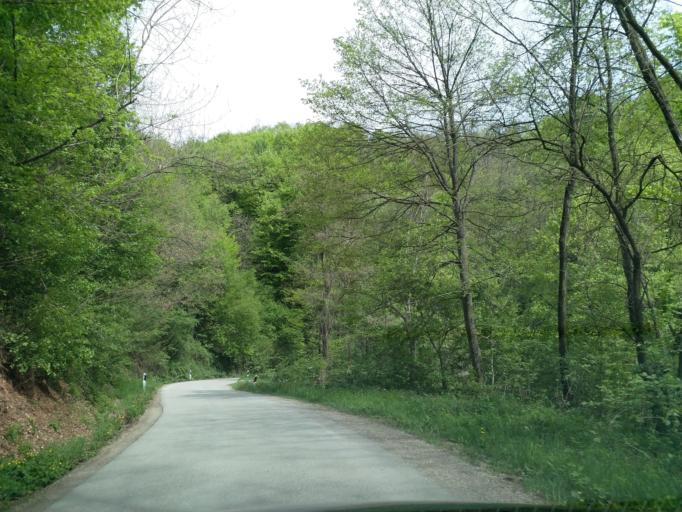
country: RS
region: Central Serbia
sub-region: Pomoravski Okrug
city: Despotovac
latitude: 43.9663
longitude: 21.5589
